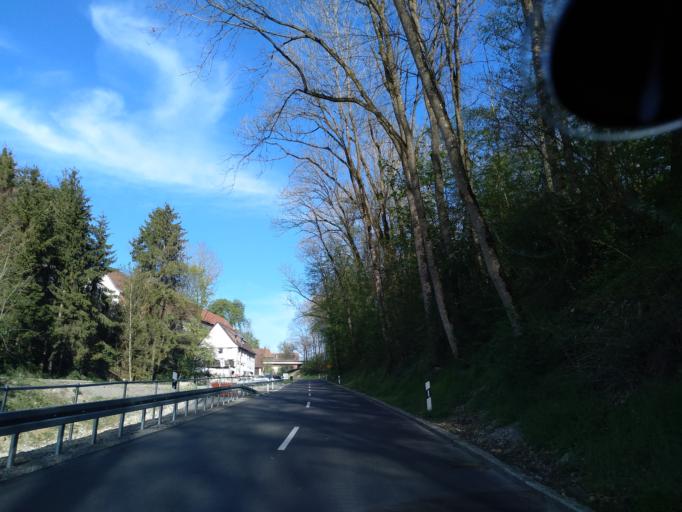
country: DE
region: Baden-Wuerttemberg
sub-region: Regierungsbezirk Stuttgart
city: Braunsbach
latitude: 49.2101
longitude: 9.8113
